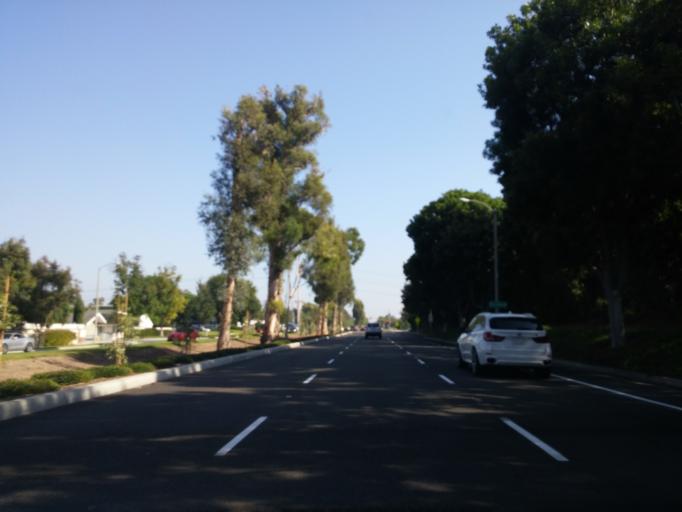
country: US
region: California
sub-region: Orange County
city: Irvine
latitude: 33.6810
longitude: -117.7811
